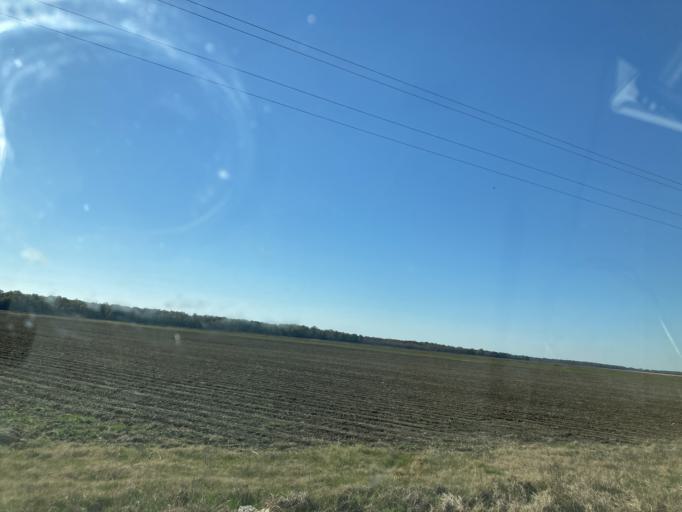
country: US
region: Mississippi
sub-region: Yazoo County
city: Yazoo City
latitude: 32.9167
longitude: -90.4495
